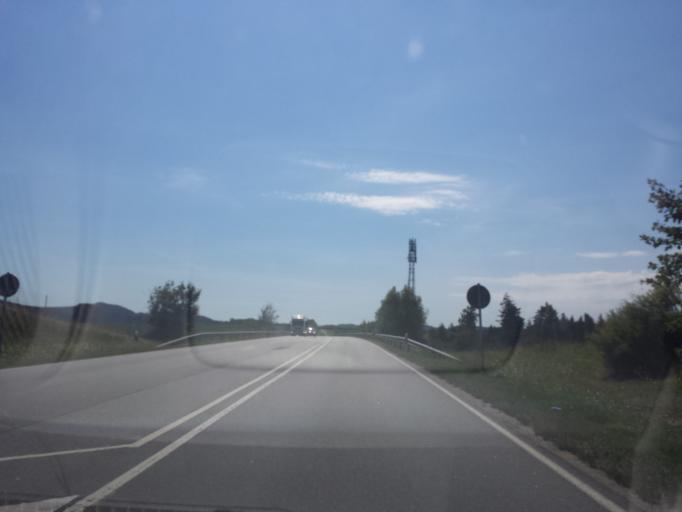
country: DE
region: Bavaria
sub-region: Upper Palatinate
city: Traitsching
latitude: 49.1634
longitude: 12.6553
